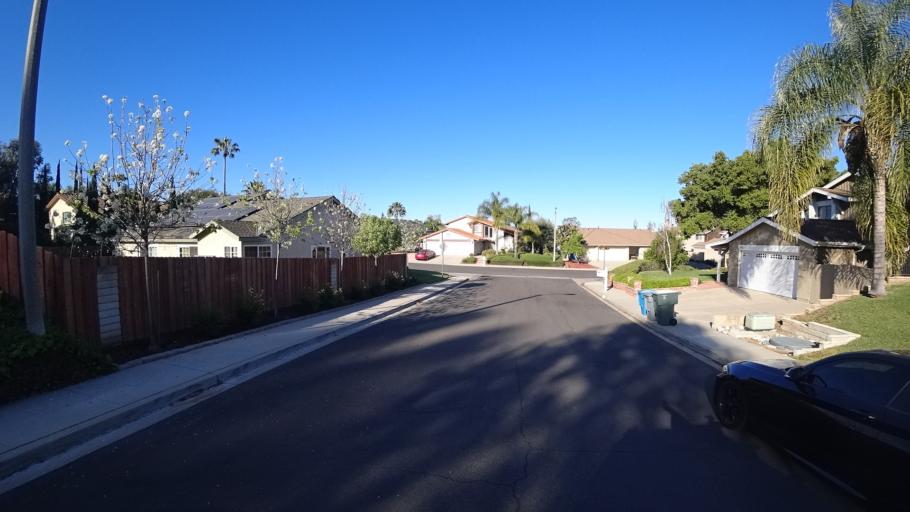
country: US
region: California
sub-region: Ventura County
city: Casa Conejo
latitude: 34.2197
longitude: -118.8908
